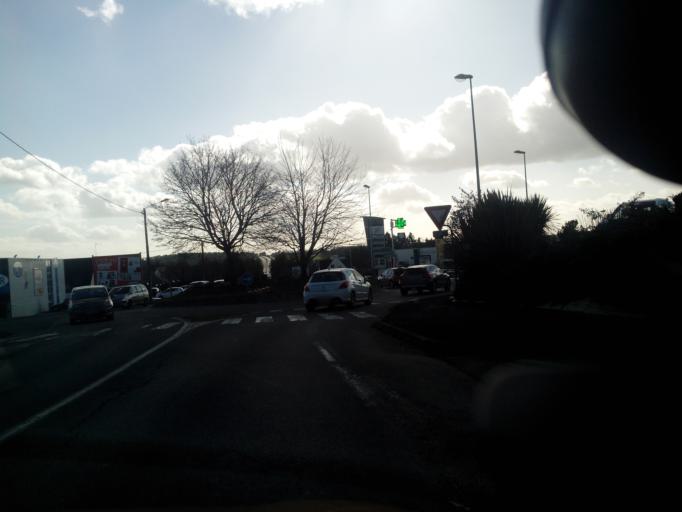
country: FR
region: Brittany
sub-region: Departement du Morbihan
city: Ploermel
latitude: 47.9249
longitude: -2.4013
